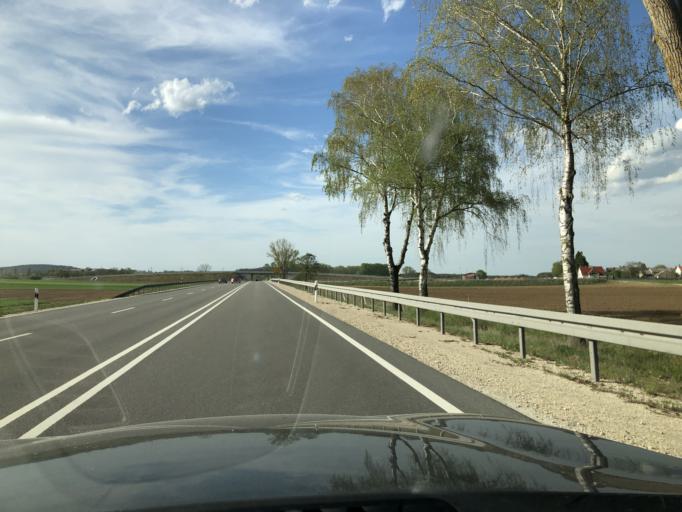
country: DE
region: Bavaria
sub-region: Regierungsbezirk Mittelfranken
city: Treuchtlingen
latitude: 48.9821
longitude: 10.9417
